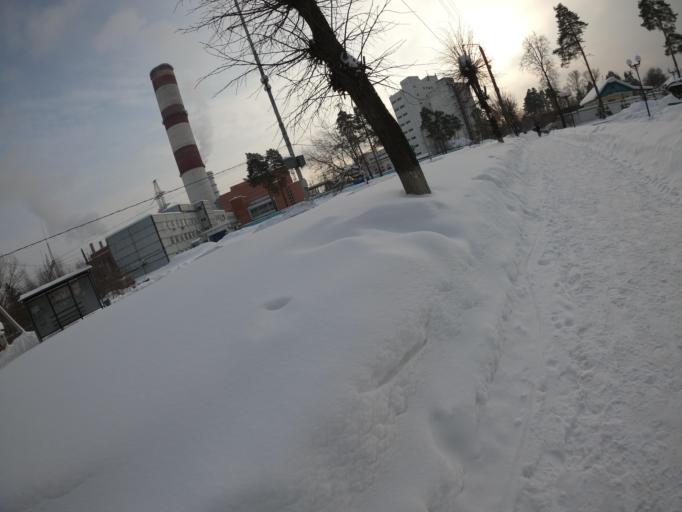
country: RU
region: Moskovskaya
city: Elektrogorsk
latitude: 55.8891
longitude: 38.7794
